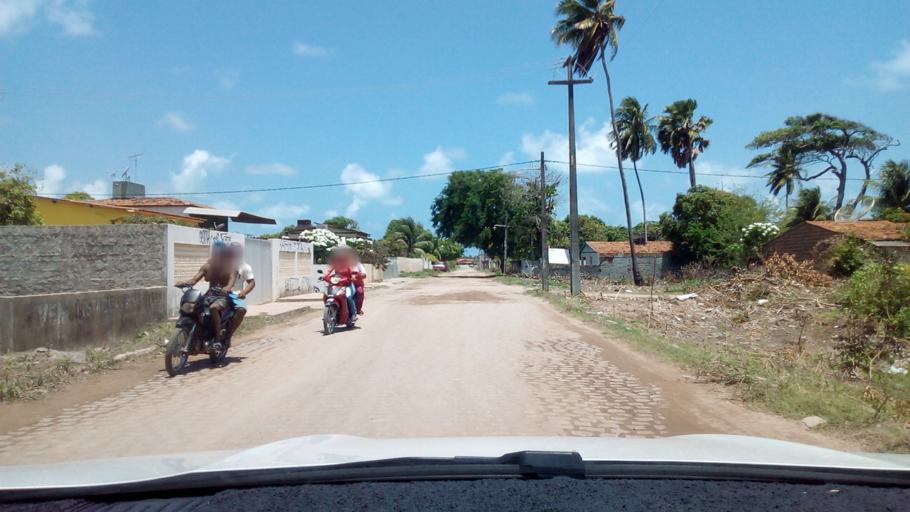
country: BR
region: Paraiba
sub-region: Pitimbu
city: Pitimbu
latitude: -7.5238
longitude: -34.8185
